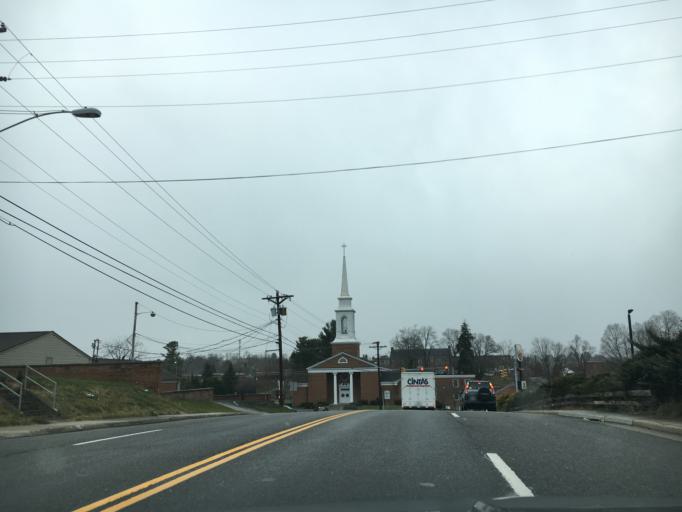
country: US
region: Virginia
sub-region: Montgomery County
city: Christiansburg
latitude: 37.1266
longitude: -80.4113
